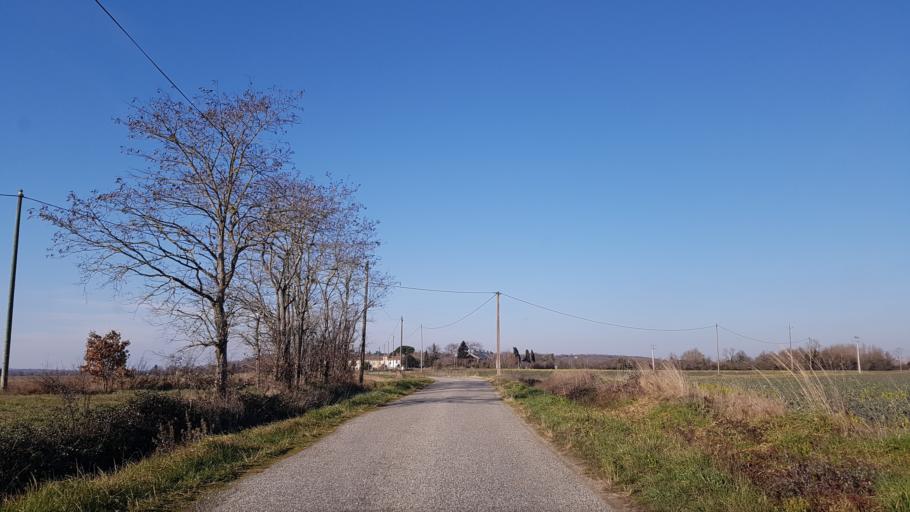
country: FR
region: Midi-Pyrenees
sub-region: Departement de l'Ariege
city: La Tour-du-Crieu
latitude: 43.1763
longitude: 1.6552
